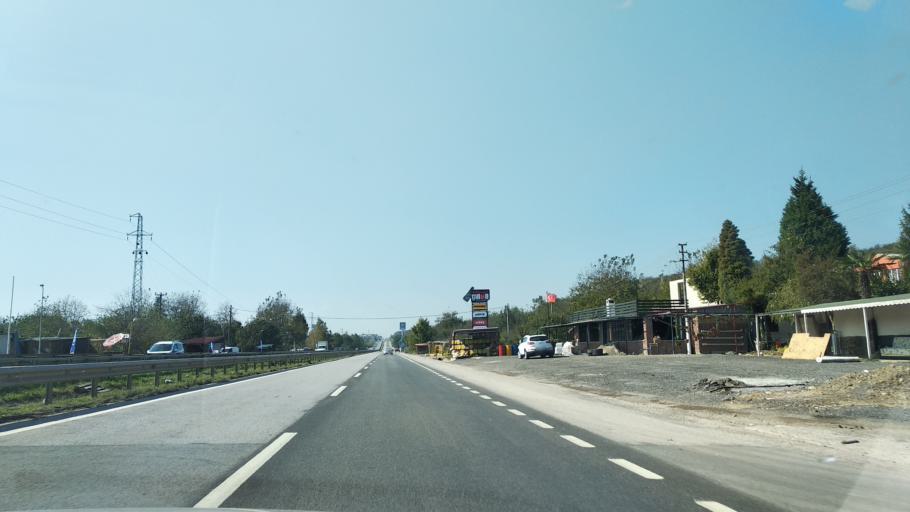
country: TR
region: Kocaeli
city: Derbent
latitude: 40.7323
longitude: 30.1920
